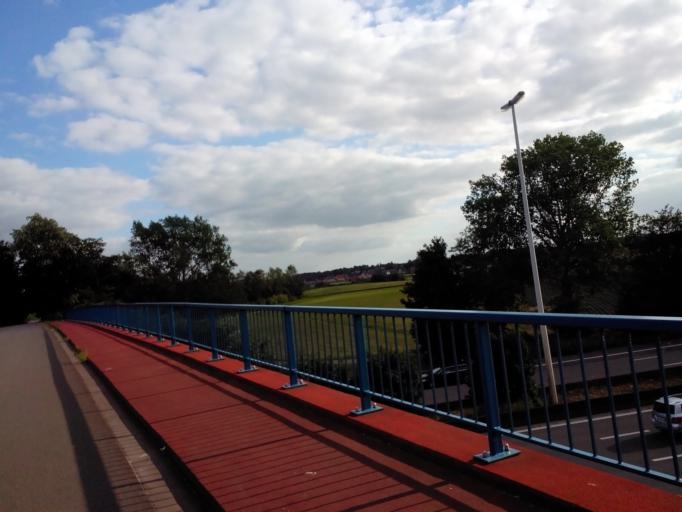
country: BE
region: Flanders
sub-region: Provincie Vlaams-Brabant
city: Bierbeek
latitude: 50.8430
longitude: 4.7425
